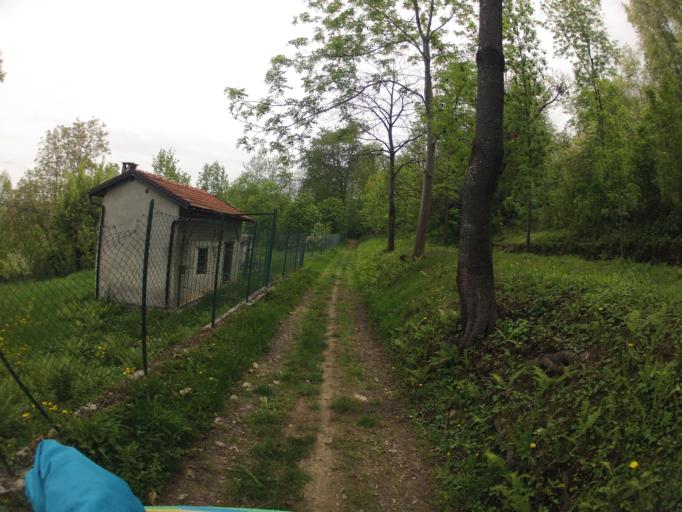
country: IT
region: Piedmont
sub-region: Provincia di Cuneo
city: Peveragno
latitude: 44.3319
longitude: 7.6070
